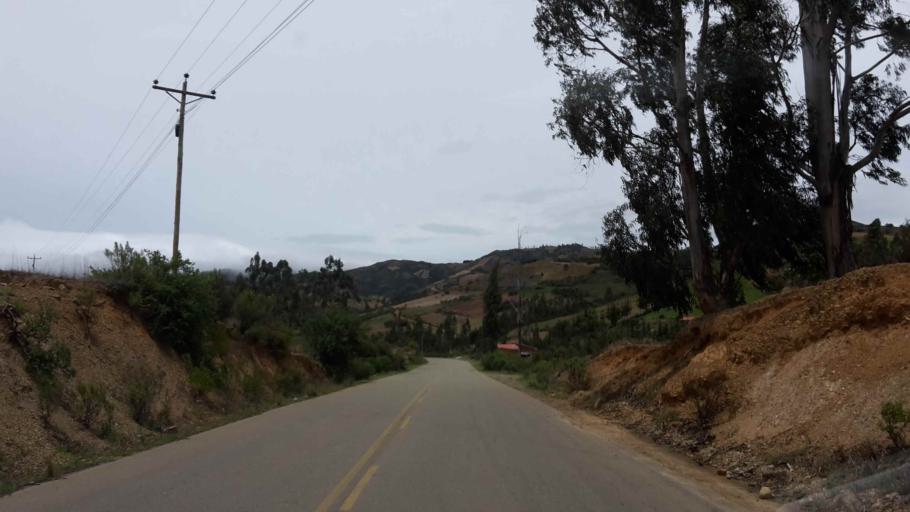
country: BO
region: Cochabamba
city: Totora
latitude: -17.6973
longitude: -65.2149
